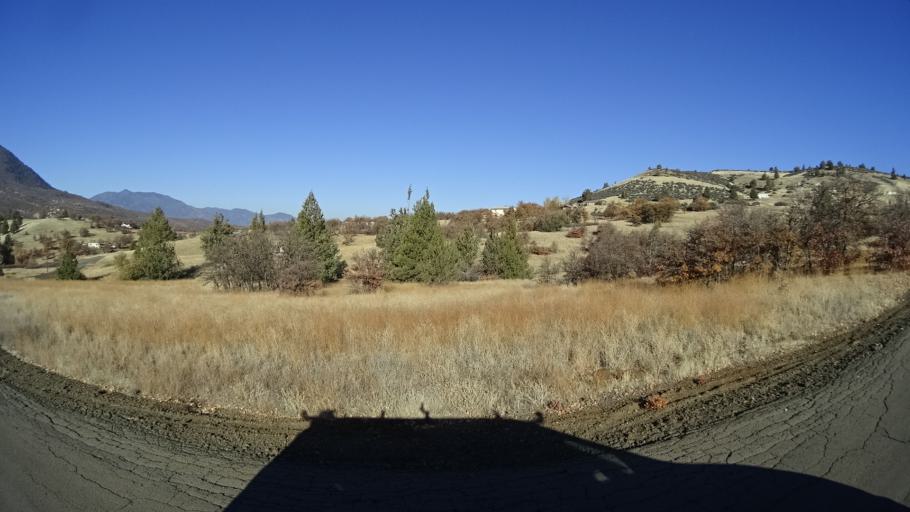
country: US
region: California
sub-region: Siskiyou County
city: Montague
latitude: 41.8759
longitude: -122.4640
